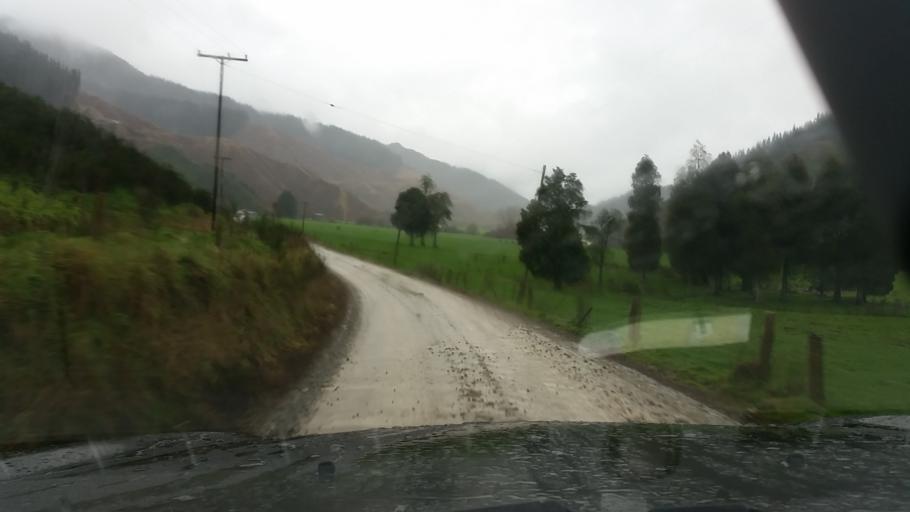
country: NZ
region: Marlborough
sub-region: Marlborough District
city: Picton
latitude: -41.3362
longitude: 173.9312
